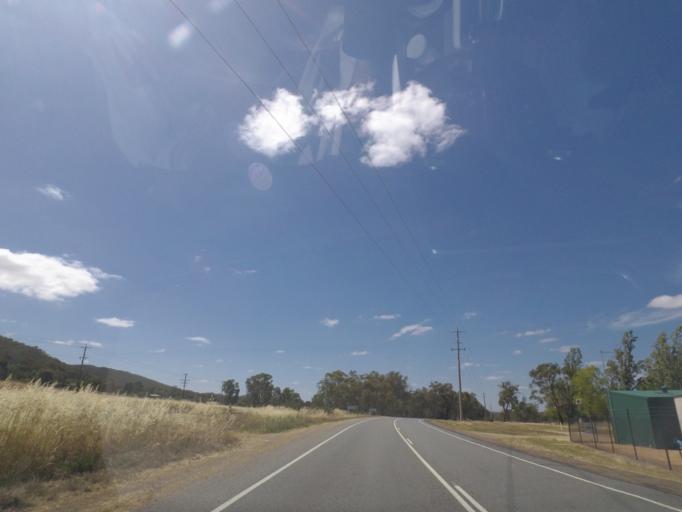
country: AU
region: Victoria
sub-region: Wangaratta
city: Wangaratta
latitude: -36.4512
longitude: 146.2381
